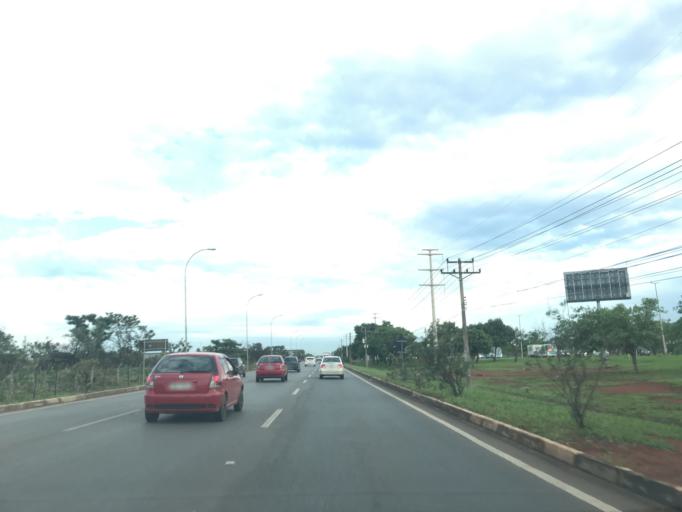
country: BR
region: Federal District
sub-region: Brasilia
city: Brasilia
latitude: -15.7842
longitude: -47.9416
